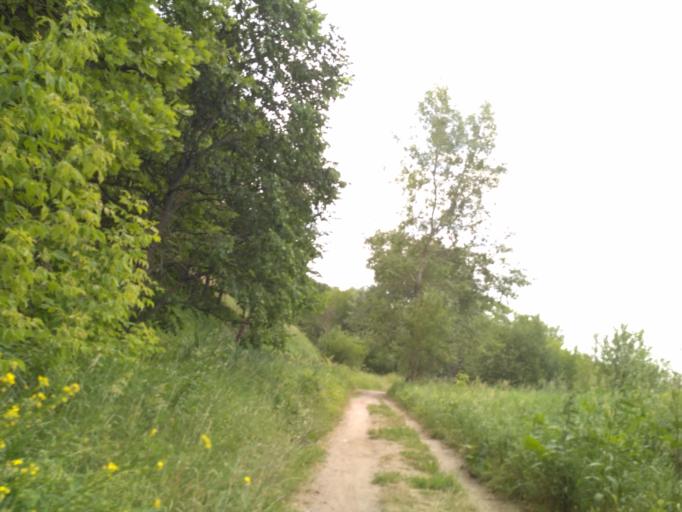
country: RU
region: Nizjnij Novgorod
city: Nizhniy Novgorod
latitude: 56.2720
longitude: 43.9722
